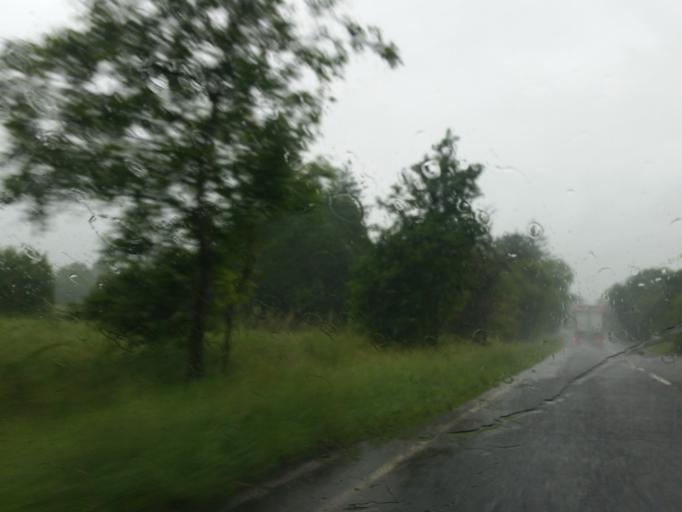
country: GB
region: Northern Ireland
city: Fivemiletown
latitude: 54.4074
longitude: -7.1785
